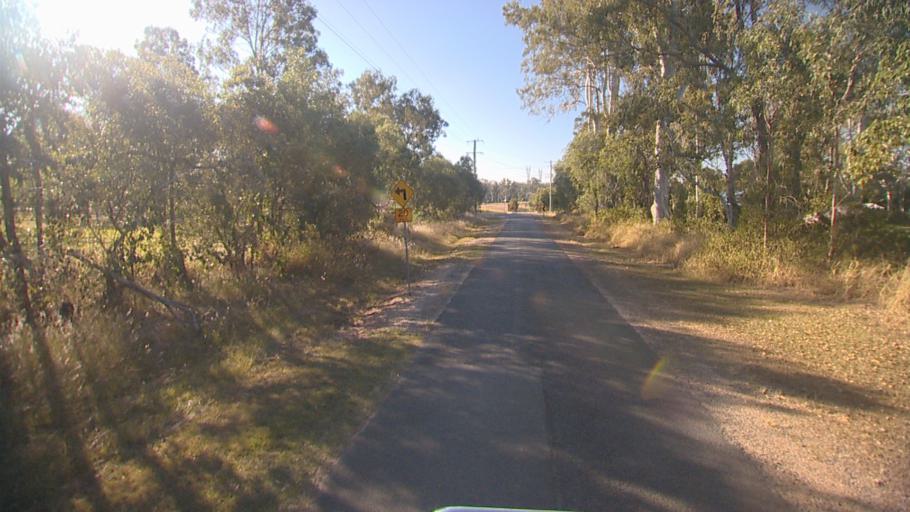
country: AU
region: Queensland
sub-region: Logan
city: North Maclean
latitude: -27.7796
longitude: 153.0402
